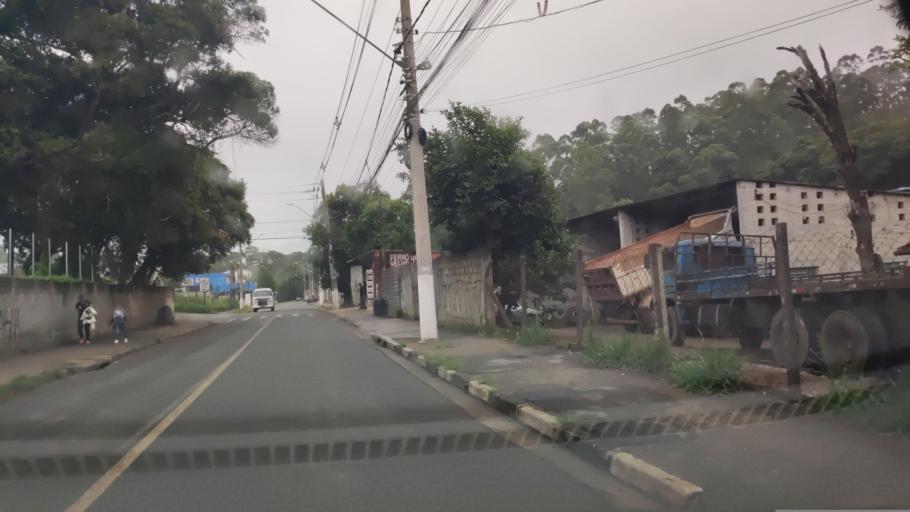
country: BR
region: Sao Paulo
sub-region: Vargem Grande Paulista
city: Vargem Grande Paulista
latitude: -23.6814
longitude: -47.0282
